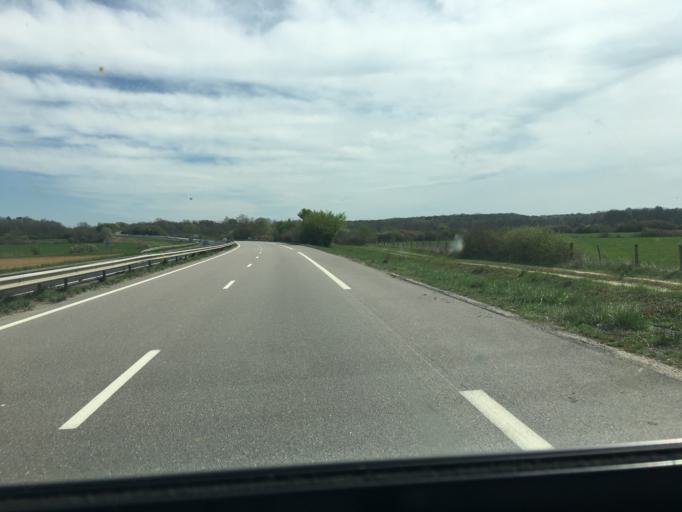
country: FR
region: Lorraine
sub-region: Departement de Meurthe-et-Moselle
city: Domgermain
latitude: 48.6505
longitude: 5.8548
